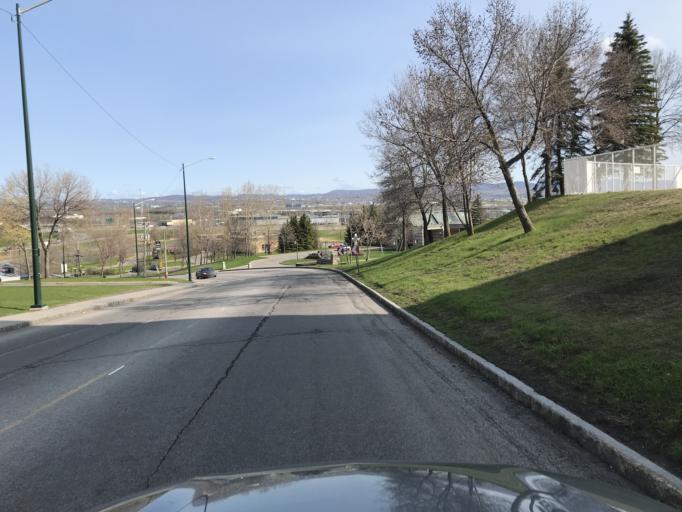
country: CA
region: Quebec
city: L'Ancienne-Lorette
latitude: 46.7905
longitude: -71.2833
